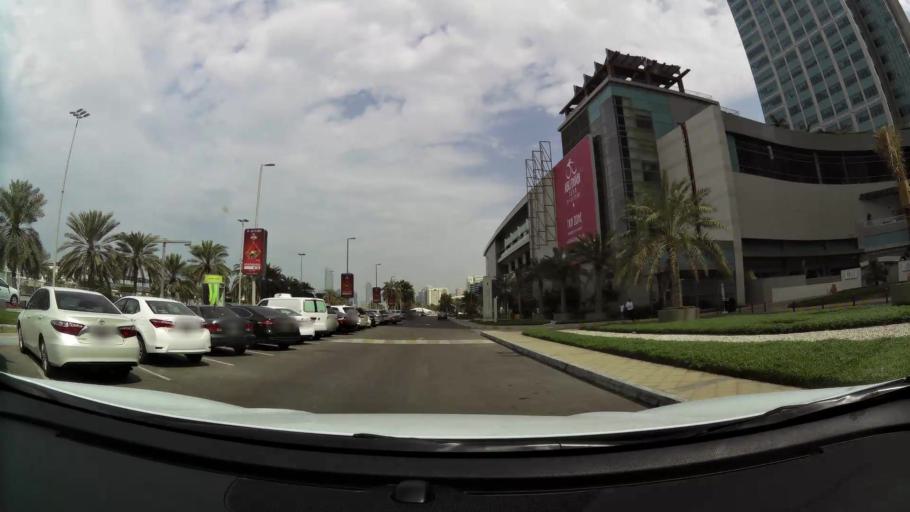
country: AE
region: Abu Dhabi
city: Abu Dhabi
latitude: 24.4646
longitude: 54.3274
